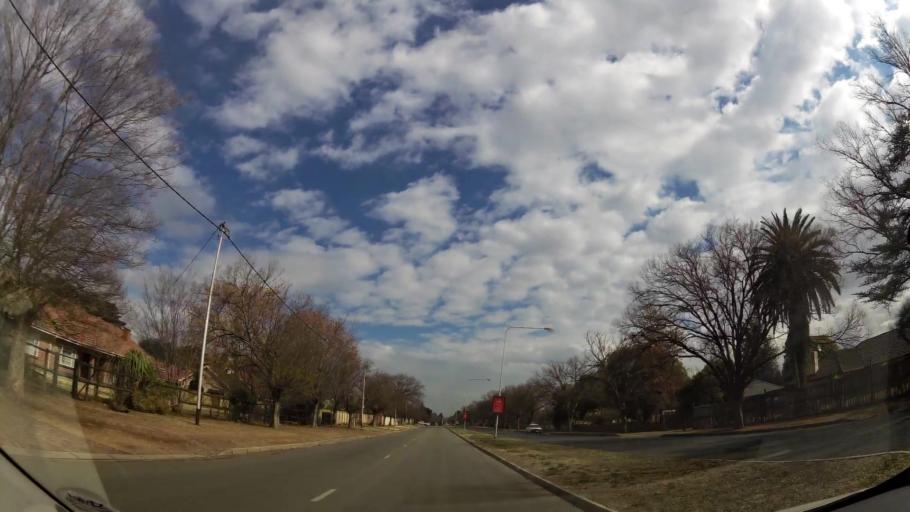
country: ZA
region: Gauteng
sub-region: Sedibeng District Municipality
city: Vereeniging
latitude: -26.6593
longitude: 27.9863
